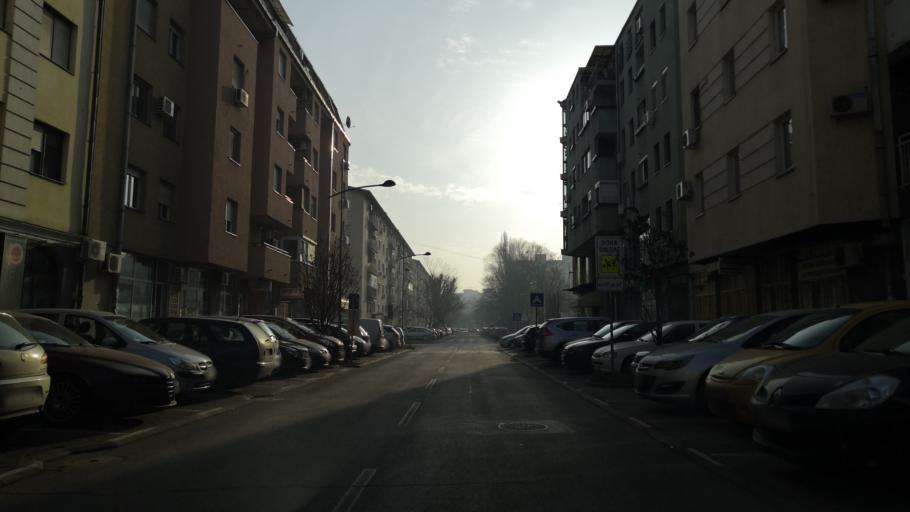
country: RS
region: Autonomna Pokrajina Vojvodina
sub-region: Juznobacki Okrug
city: Novi Sad
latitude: 45.2451
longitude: 19.8329
